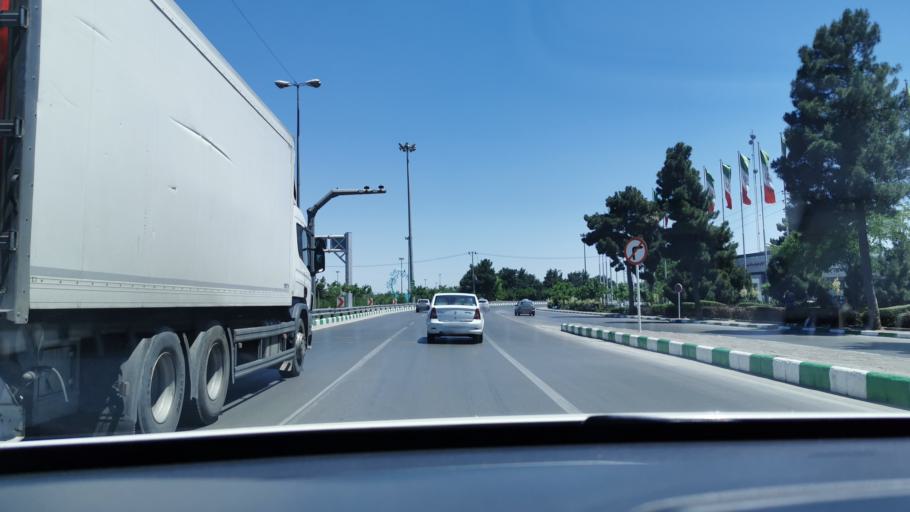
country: IR
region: Razavi Khorasan
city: Mashhad
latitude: 36.2531
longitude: 59.6048
